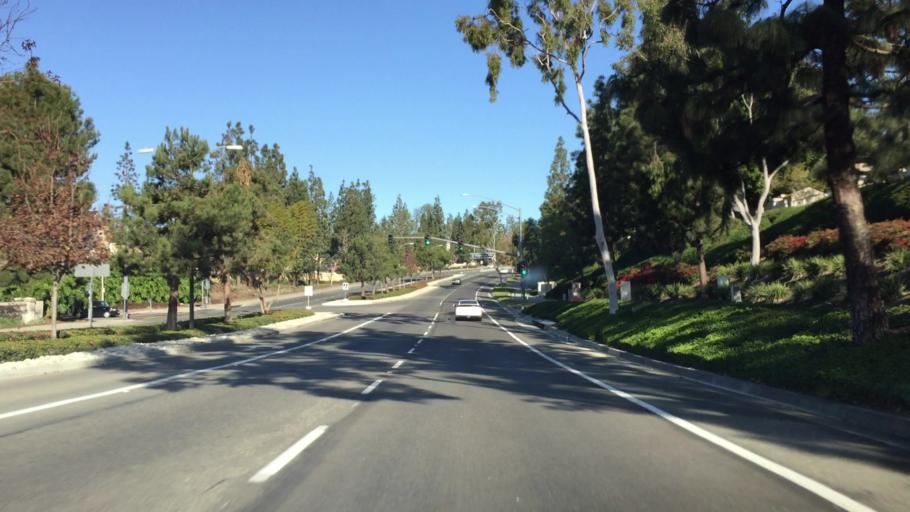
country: US
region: California
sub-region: Orange County
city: Laguna Niguel
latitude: 33.5179
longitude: -117.6831
